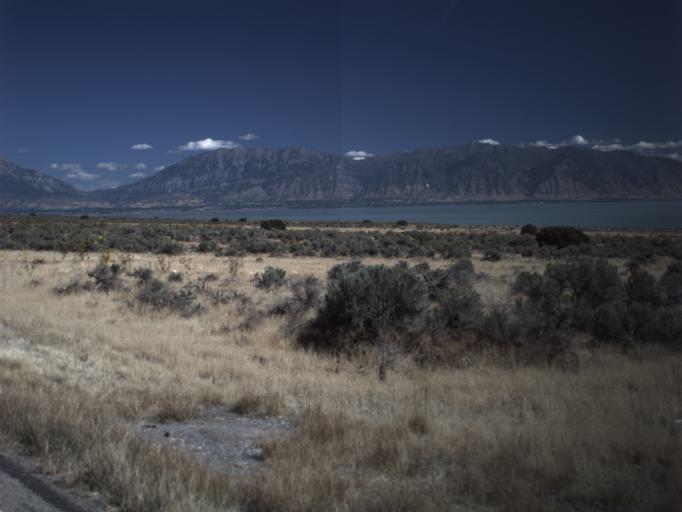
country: US
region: Utah
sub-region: Utah County
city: Saratoga Springs
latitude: 40.2053
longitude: -111.8958
